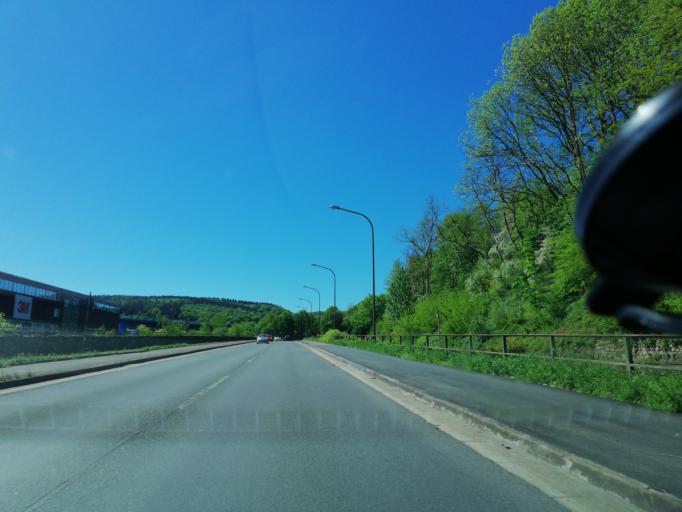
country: DE
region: North Rhine-Westphalia
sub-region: Regierungsbezirk Arnsberg
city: Schwelm
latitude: 51.2630
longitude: 7.2331
